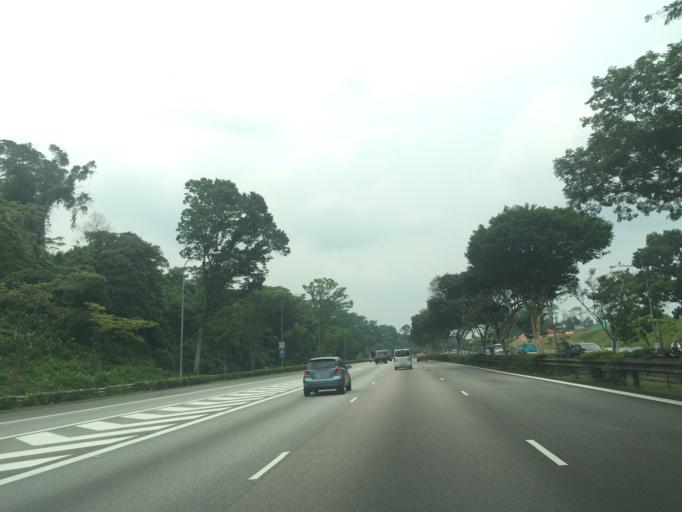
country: MY
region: Johor
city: Johor Bahru
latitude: 1.3893
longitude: 103.7593
